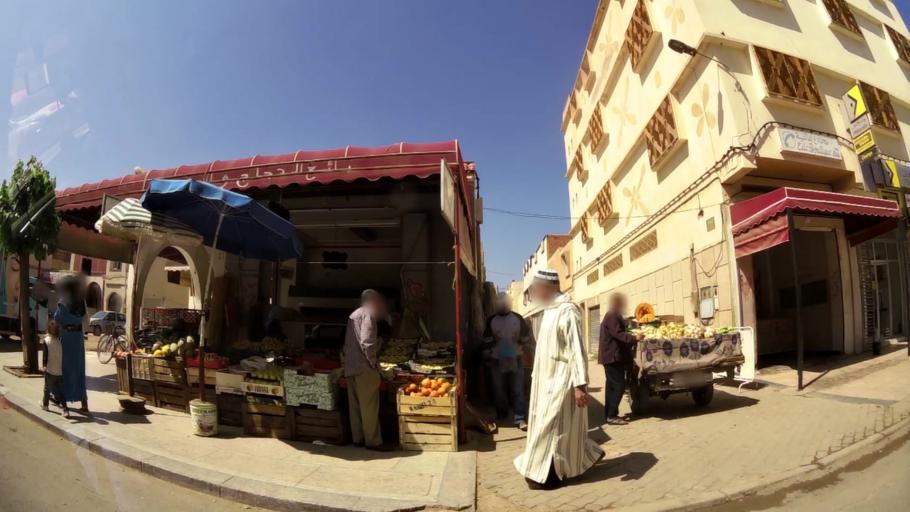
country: MA
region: Oriental
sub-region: Oujda-Angad
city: Oujda
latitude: 34.6714
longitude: -1.9392
